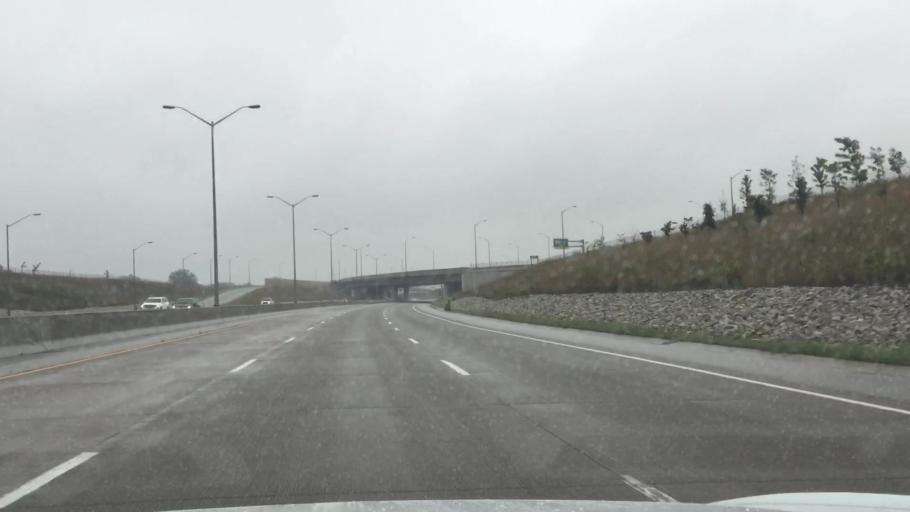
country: CA
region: Ontario
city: Windsor
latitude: 42.2396
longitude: -83.0071
